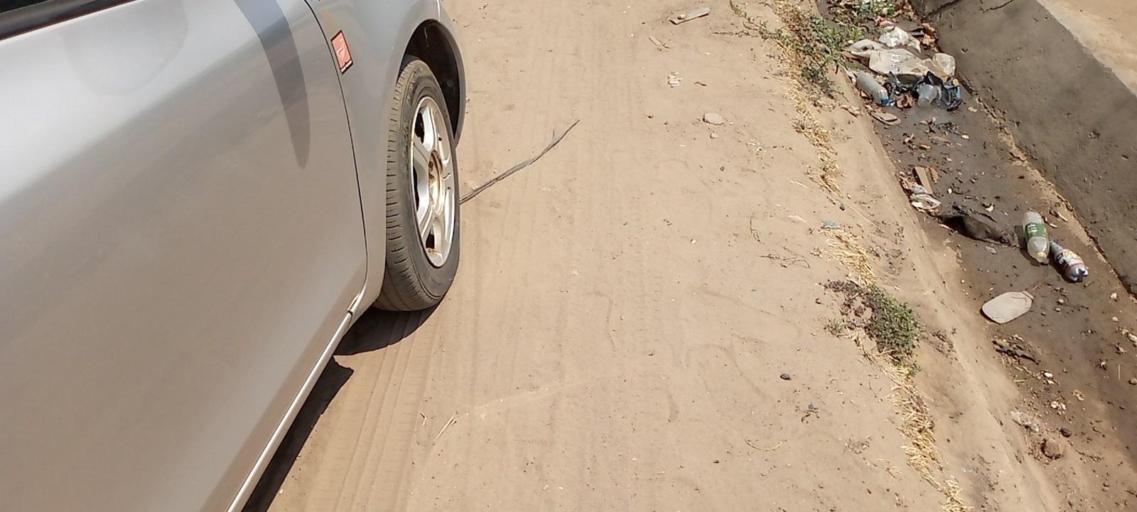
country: ZM
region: Lusaka
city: Lusaka
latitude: -15.4055
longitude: 28.3507
